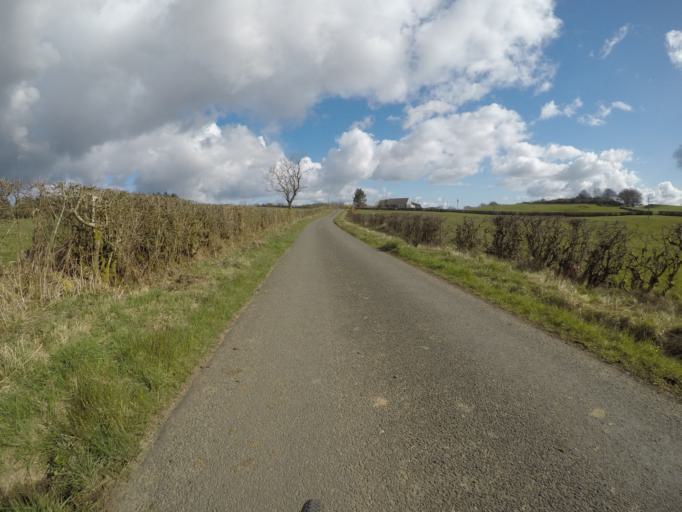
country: GB
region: Scotland
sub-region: North Ayrshire
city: Beith
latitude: 55.7059
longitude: -4.6633
